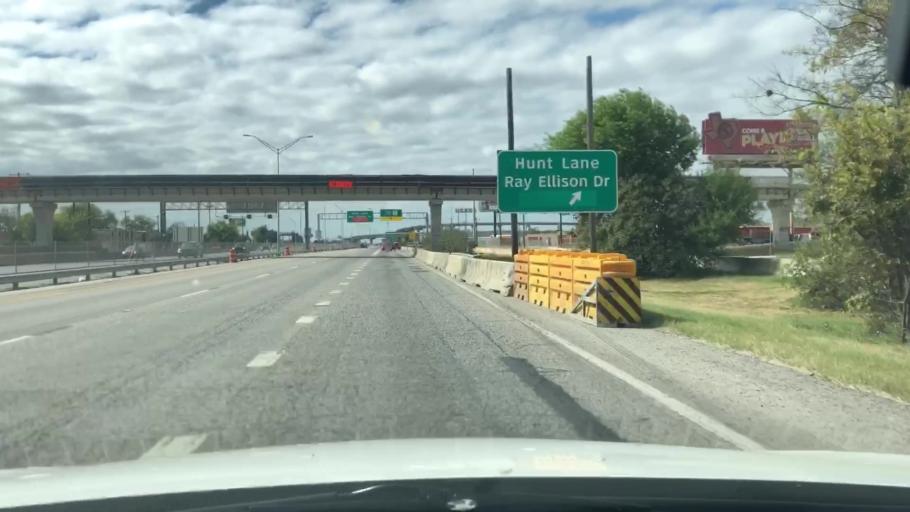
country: US
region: Texas
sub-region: Bexar County
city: Lackland Air Force Base
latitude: 29.3998
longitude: -98.6401
